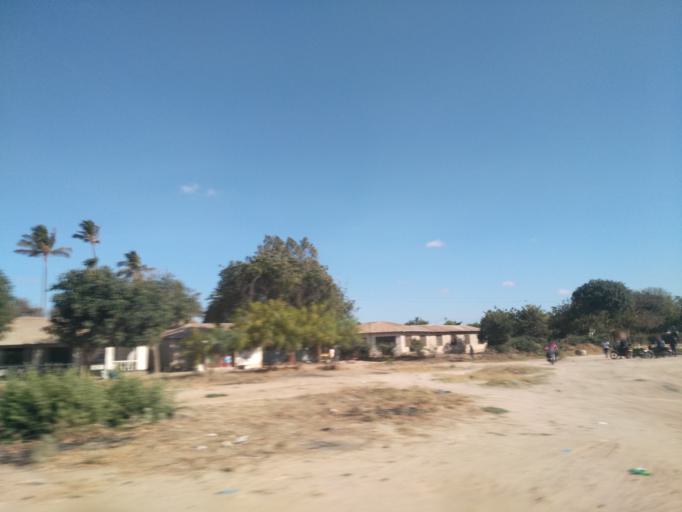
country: TZ
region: Dodoma
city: Dodoma
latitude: -6.1866
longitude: 35.7360
